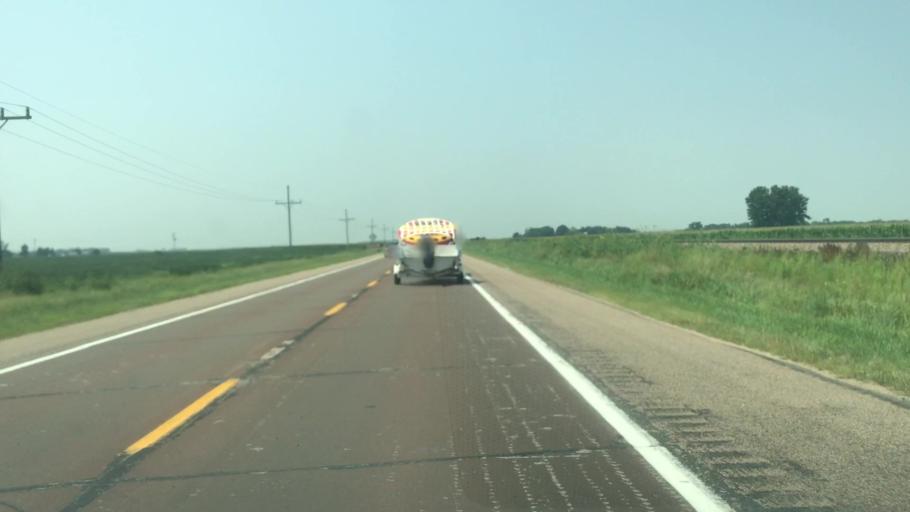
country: US
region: Nebraska
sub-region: Hall County
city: Grand Island
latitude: 40.9620
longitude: -98.4227
